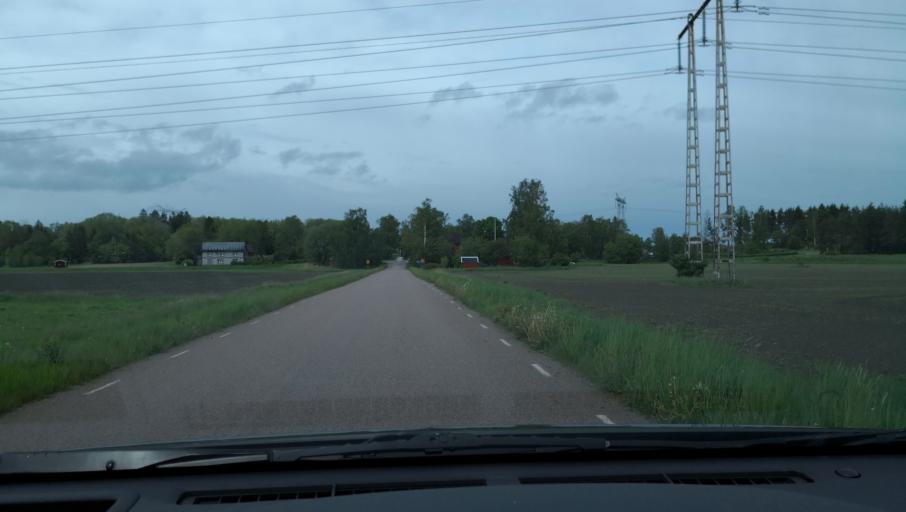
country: SE
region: Uppsala
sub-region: Enkopings Kommun
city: Orsundsbro
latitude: 59.6863
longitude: 17.3796
